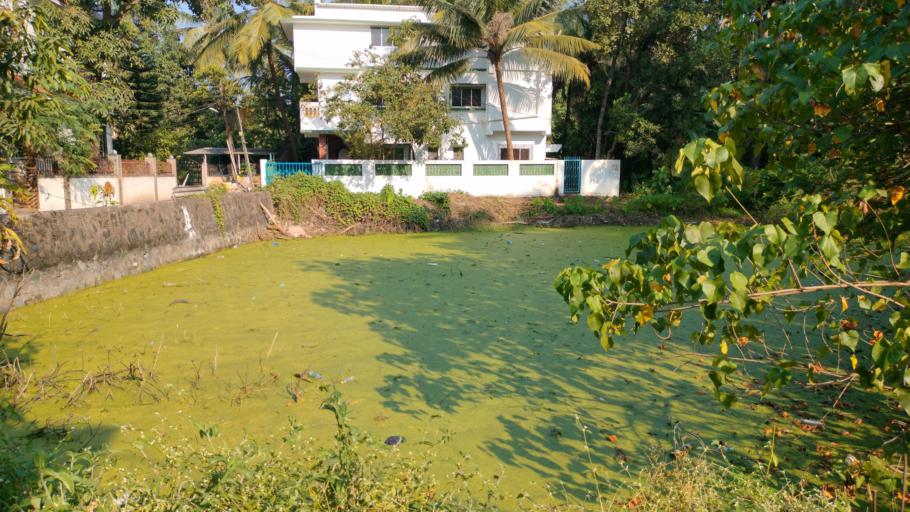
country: IN
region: Maharashtra
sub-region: Thane
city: Bhayandar
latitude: 19.3573
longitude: 72.7912
